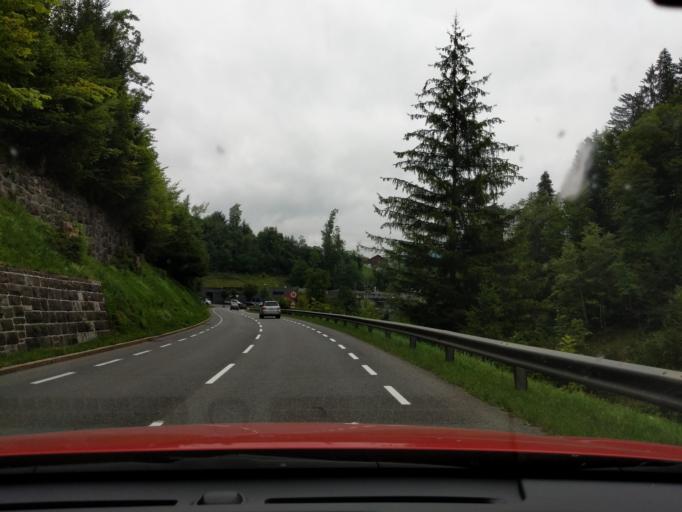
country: AT
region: Vorarlberg
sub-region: Politischer Bezirk Bregenz
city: Egg
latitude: 47.4349
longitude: 9.8905
